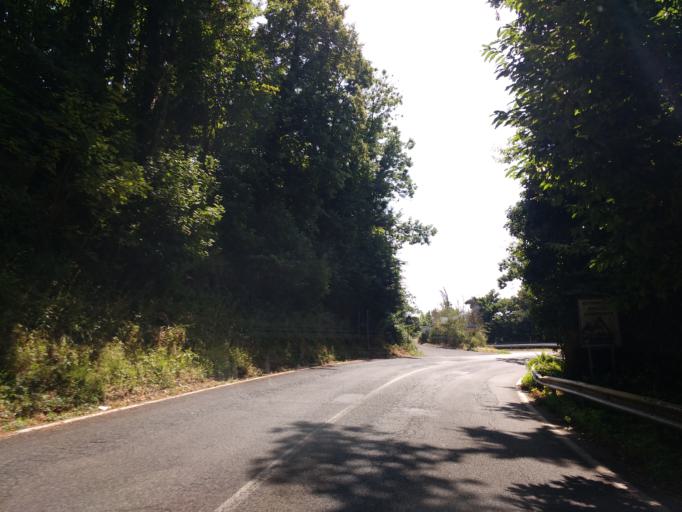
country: IT
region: Latium
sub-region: Citta metropolitana di Roma Capitale
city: Rocca di Papa
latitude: 41.7500
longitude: 12.6983
